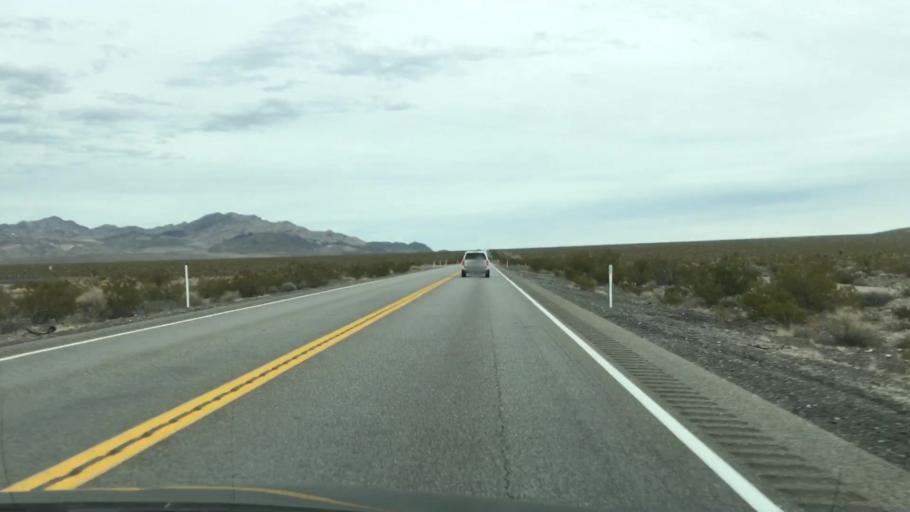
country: US
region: Nevada
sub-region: Nye County
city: Pahrump
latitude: 36.5904
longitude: -116.0396
